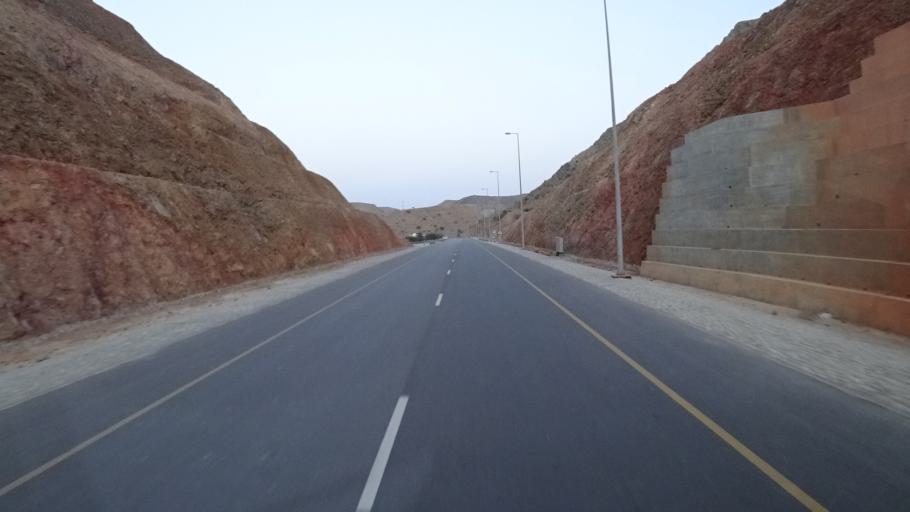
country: OM
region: Muhafazat Masqat
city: Muscat
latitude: 23.5081
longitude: 58.7257
